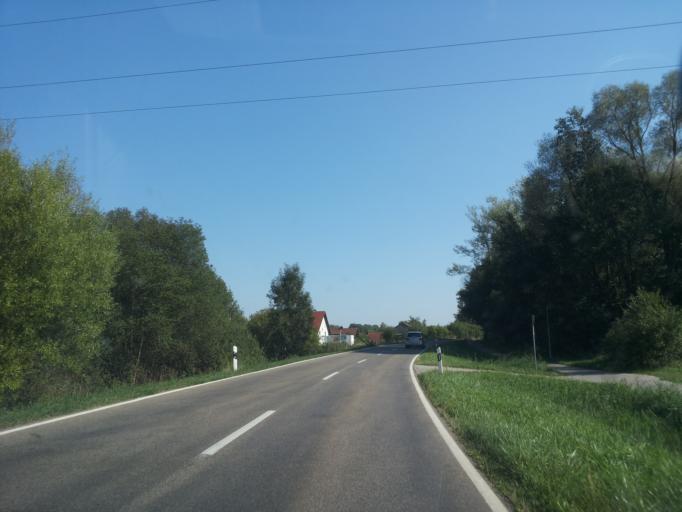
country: DE
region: Bavaria
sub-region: Lower Bavaria
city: Neustadt an der Donau
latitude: 48.8302
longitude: 11.7760
